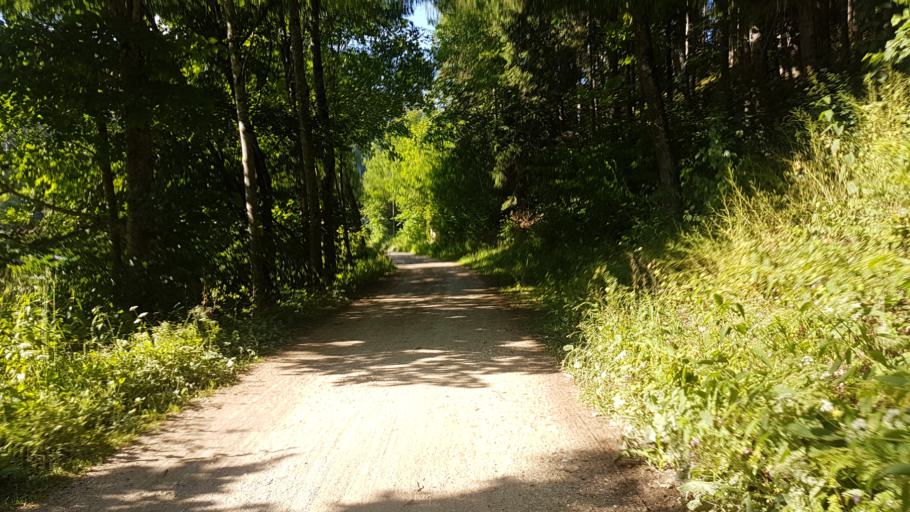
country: DE
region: Baden-Wuerttemberg
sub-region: Tuebingen Region
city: Stetten am Kalten Markt
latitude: 48.0889
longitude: 9.1018
